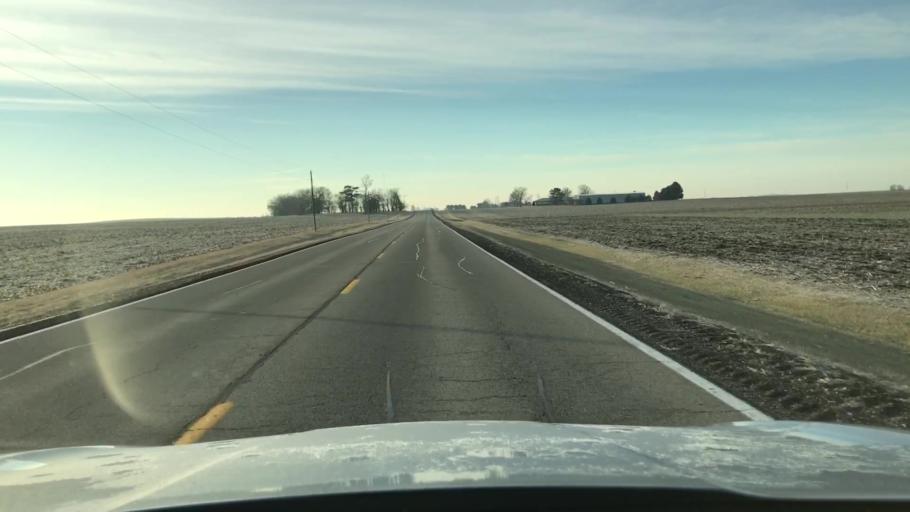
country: US
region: Illinois
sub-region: McLean County
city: Hudson
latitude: 40.5965
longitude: -88.9448
